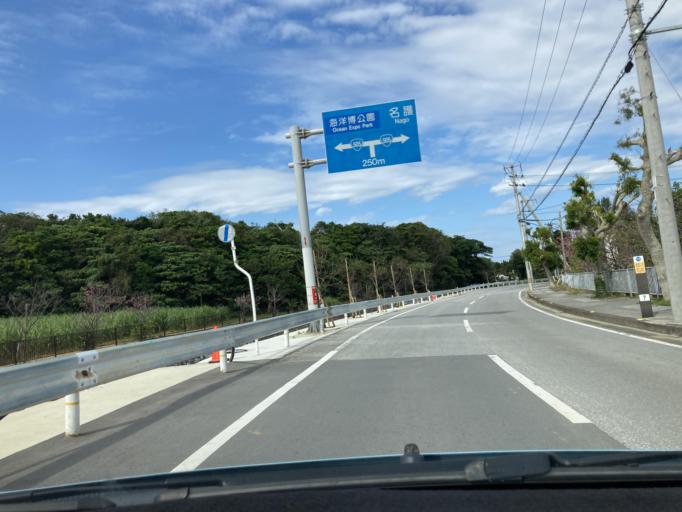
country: JP
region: Okinawa
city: Nago
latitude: 26.6992
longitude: 127.9247
